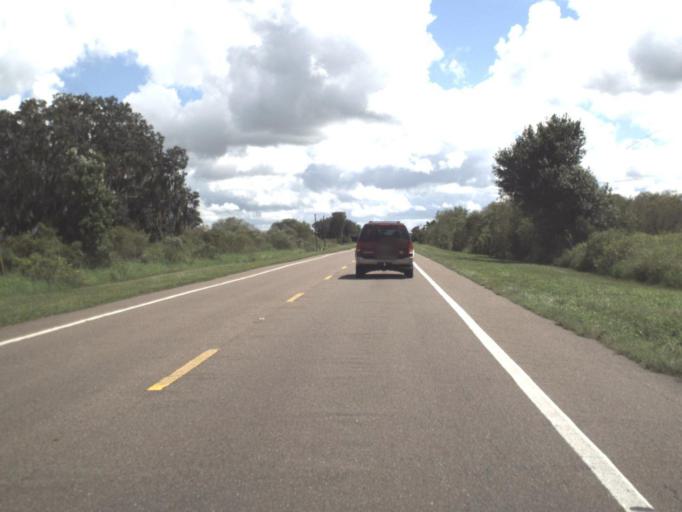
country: US
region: Florida
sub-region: DeSoto County
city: Arcadia
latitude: 27.3067
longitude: -82.0916
